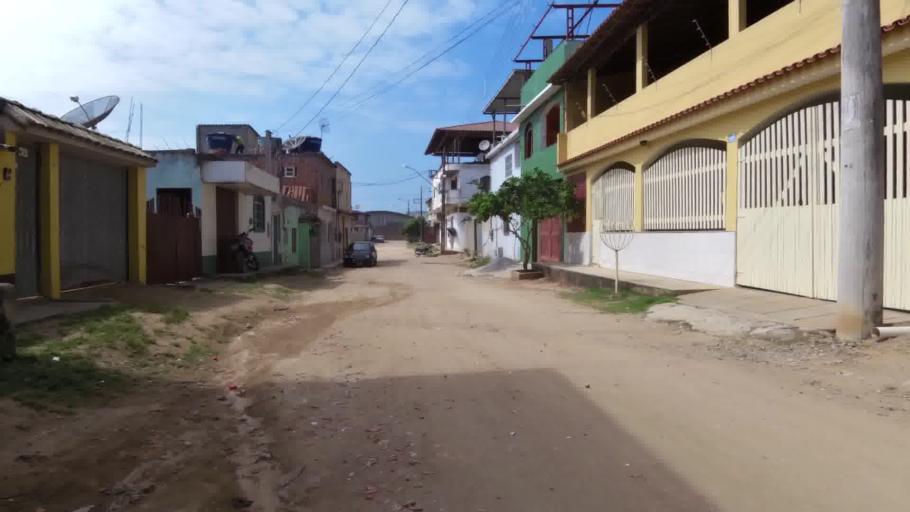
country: BR
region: Espirito Santo
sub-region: Itapemirim
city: Itapemirim
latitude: -21.0228
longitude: -40.8182
